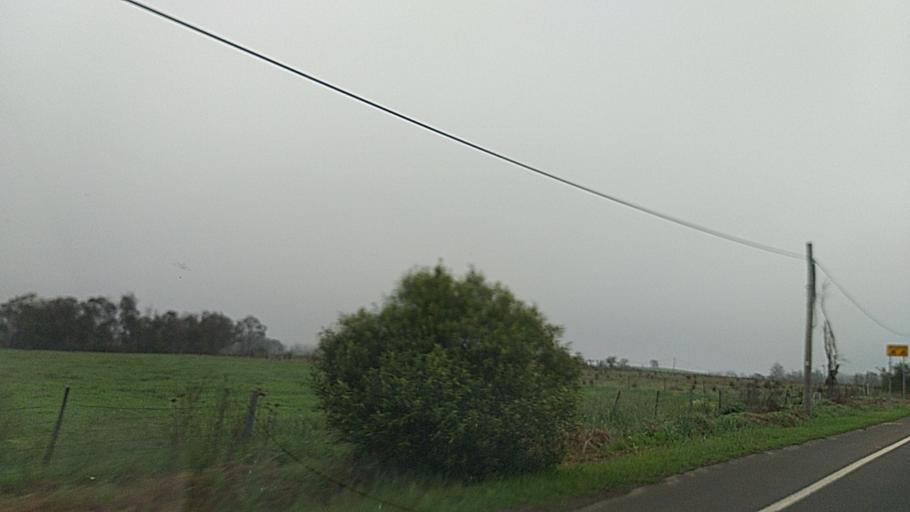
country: AU
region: New South Wales
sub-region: Liverpool
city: Luddenham
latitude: -33.9065
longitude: 150.7051
